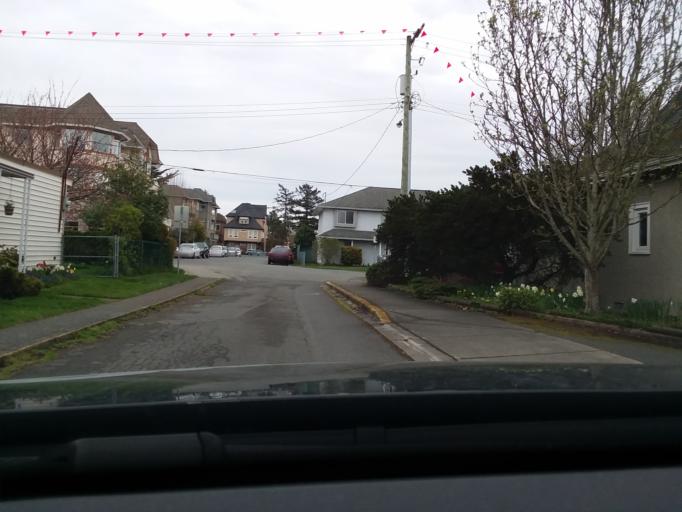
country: CA
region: British Columbia
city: North Saanich
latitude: 48.6468
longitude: -123.3983
